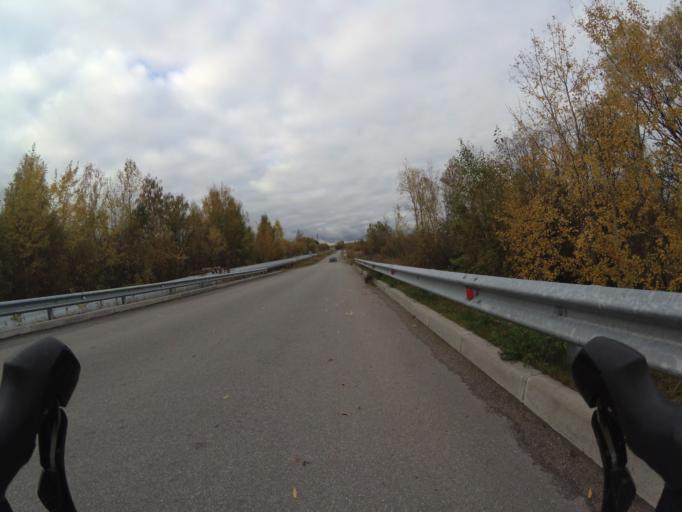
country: RU
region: St.-Petersburg
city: Lakhtinskiy
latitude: 59.9980
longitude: 30.1596
